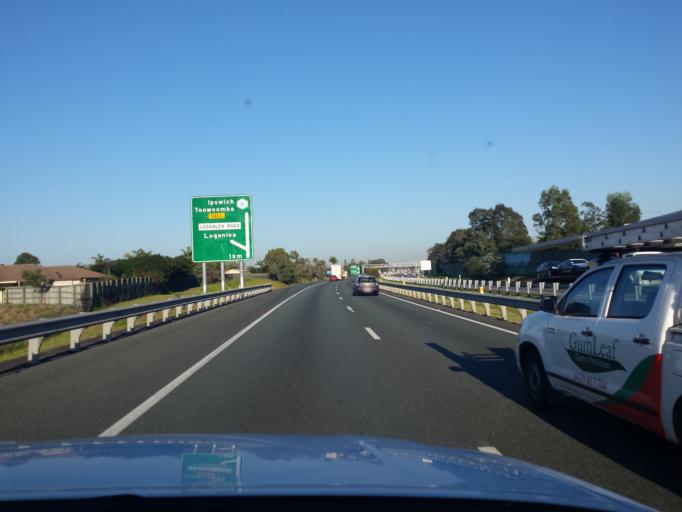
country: AU
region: Queensland
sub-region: Logan
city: Slacks Creek
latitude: -27.6670
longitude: 153.1549
